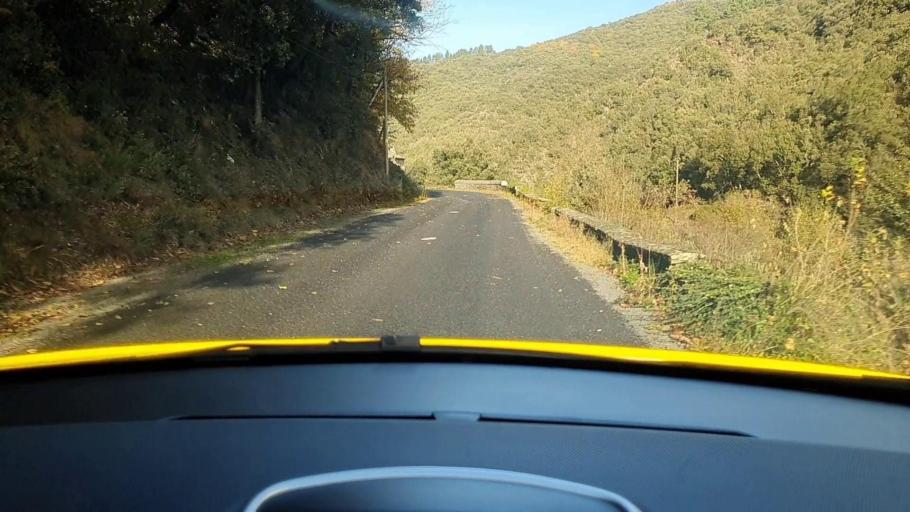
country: FR
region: Languedoc-Roussillon
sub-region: Departement du Gard
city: Valleraugue
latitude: 44.1033
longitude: 3.7327
